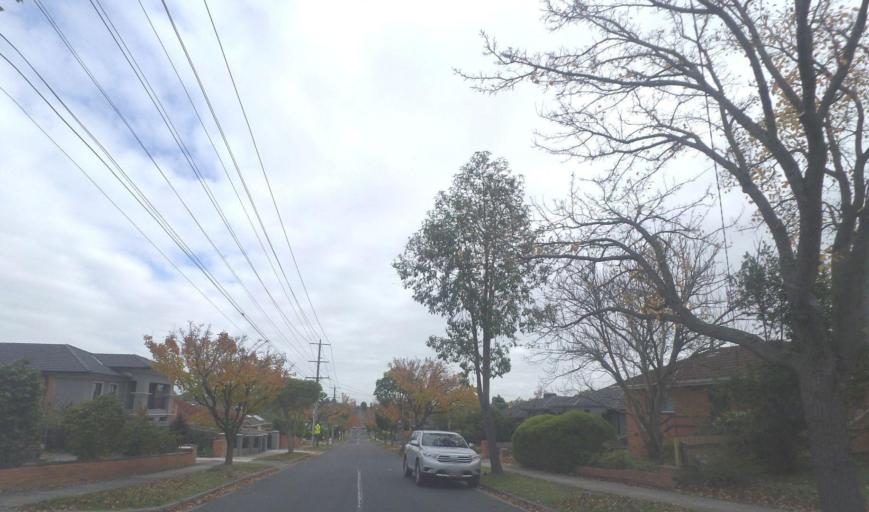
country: AU
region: Victoria
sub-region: Whitehorse
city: Blackburn North
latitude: -37.8043
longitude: 145.1516
